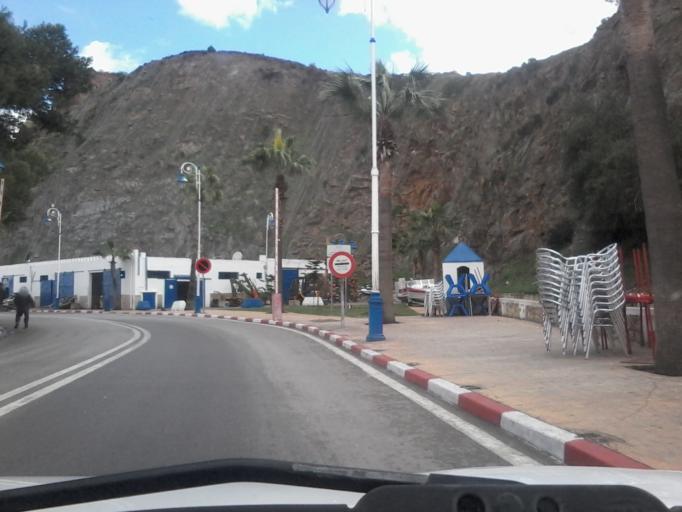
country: MA
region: Tanger-Tetouan
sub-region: Tetouan
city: Martil
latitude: 35.6811
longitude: -5.3125
